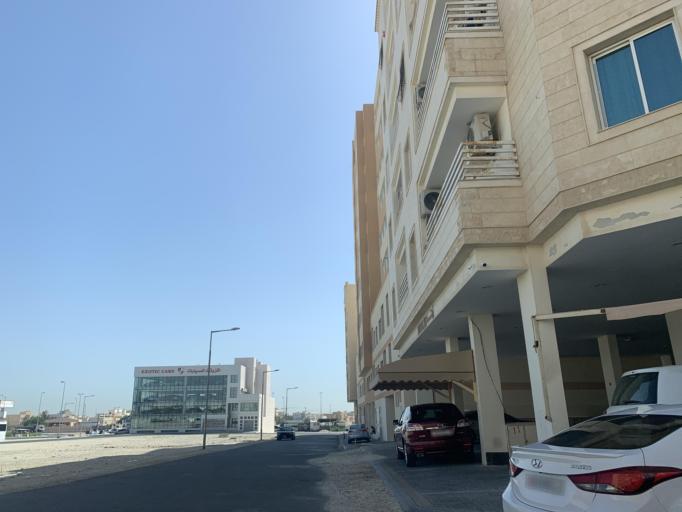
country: BH
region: Northern
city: Ar Rifa'
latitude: 26.1390
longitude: 50.5789
